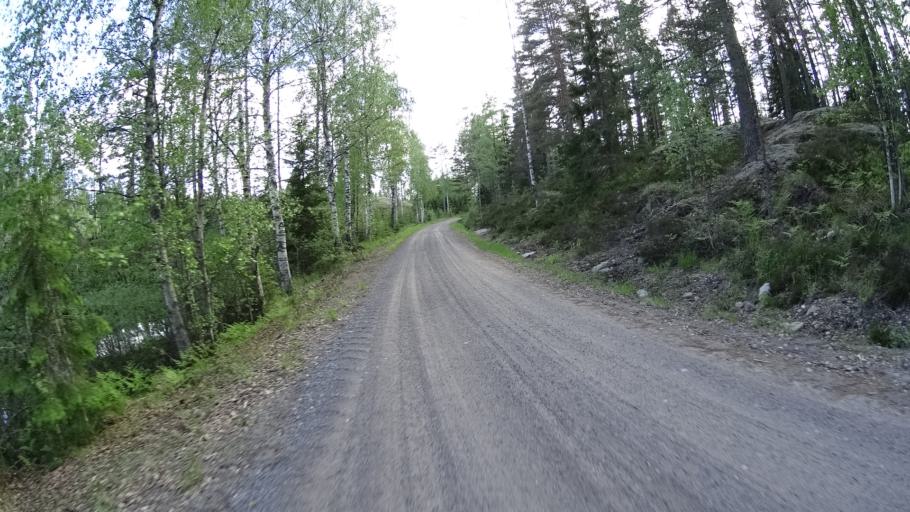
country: FI
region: Uusimaa
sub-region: Raaseporin
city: Pohja
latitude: 60.1586
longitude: 23.4914
